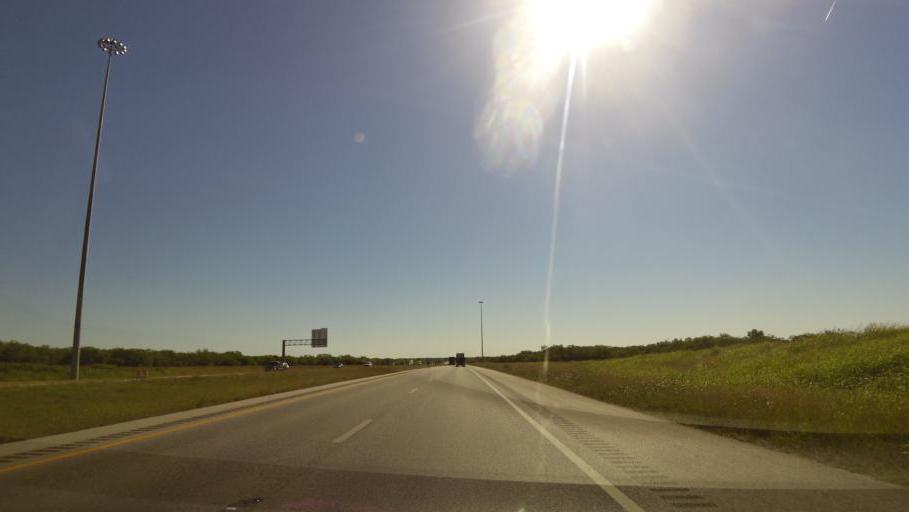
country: US
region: Texas
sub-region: Guadalupe County
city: Seguin
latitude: 29.6102
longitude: -97.8693
